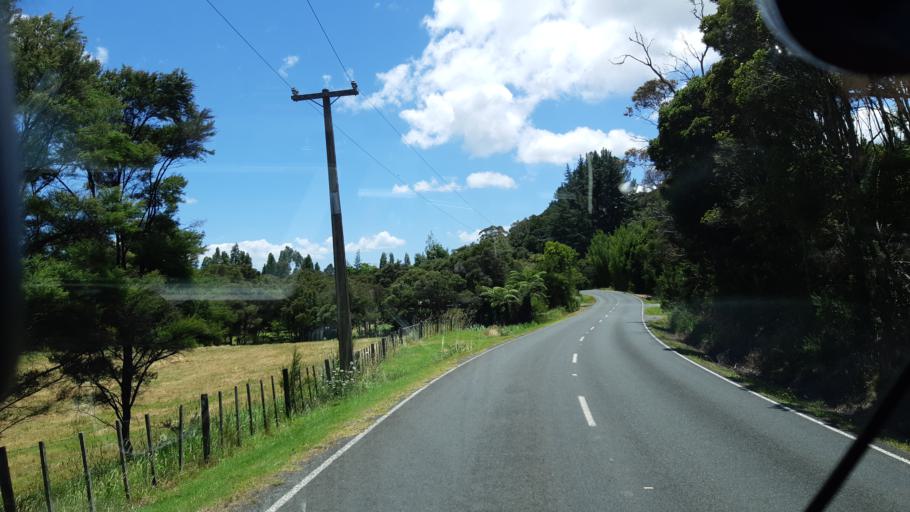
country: NZ
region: Northland
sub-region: Far North District
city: Kaitaia
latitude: -35.1629
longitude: 173.3481
